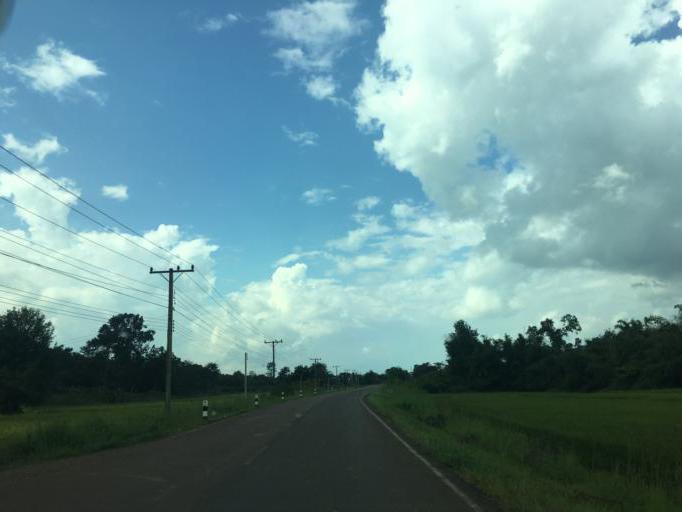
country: TH
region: Nong Khai
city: Sangkhom
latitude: 18.1813
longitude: 102.2499
